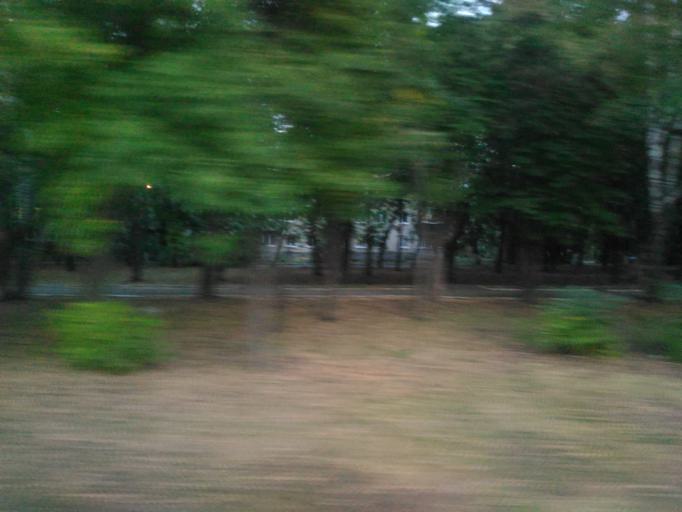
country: RU
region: Ulyanovsk
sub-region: Ulyanovskiy Rayon
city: Ulyanovsk
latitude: 54.3064
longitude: 48.3236
